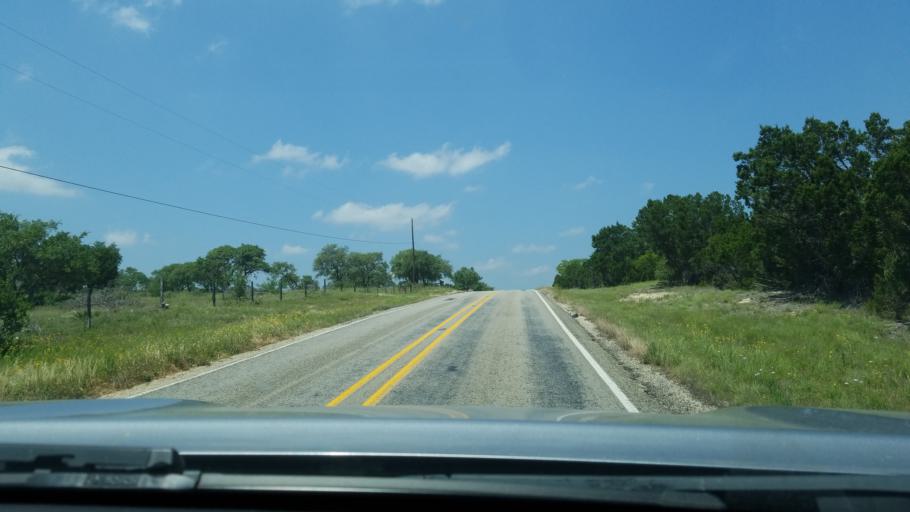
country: US
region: Texas
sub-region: Hays County
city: Woodcreek
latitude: 30.0849
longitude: -98.2280
